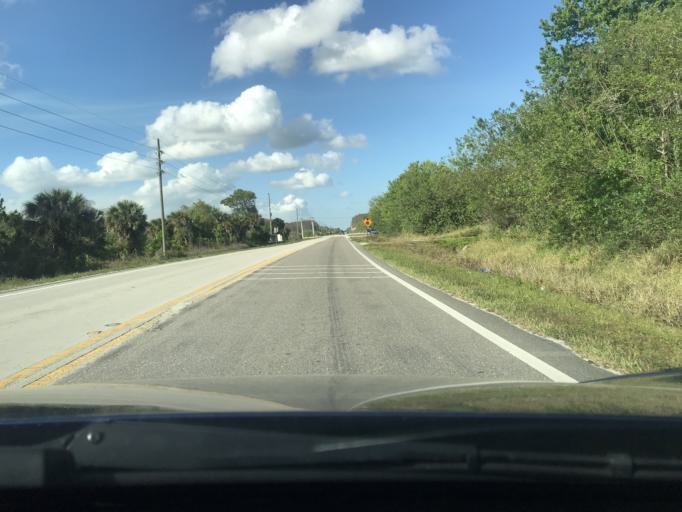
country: US
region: Florida
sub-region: Okeechobee County
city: Taylor Creek
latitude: 27.2883
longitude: -80.6973
